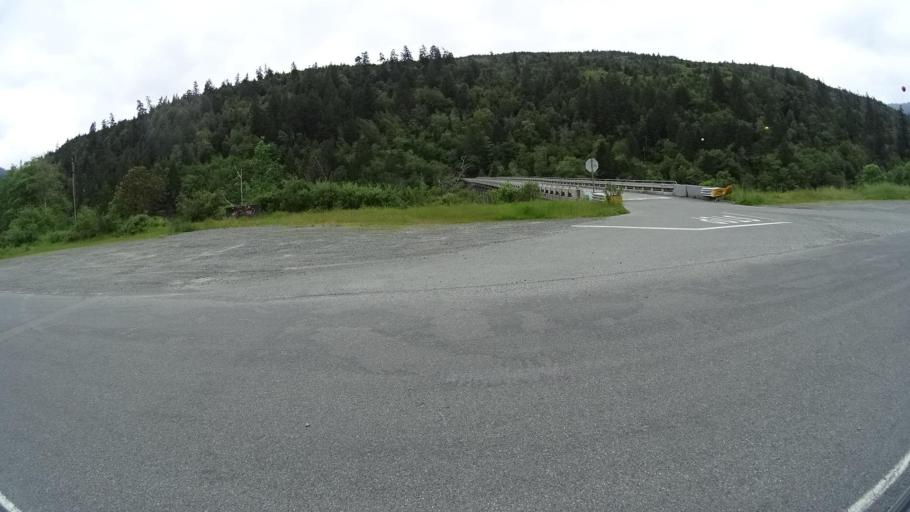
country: US
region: California
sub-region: Humboldt County
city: Willow Creek
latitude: 41.2083
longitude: -123.7550
